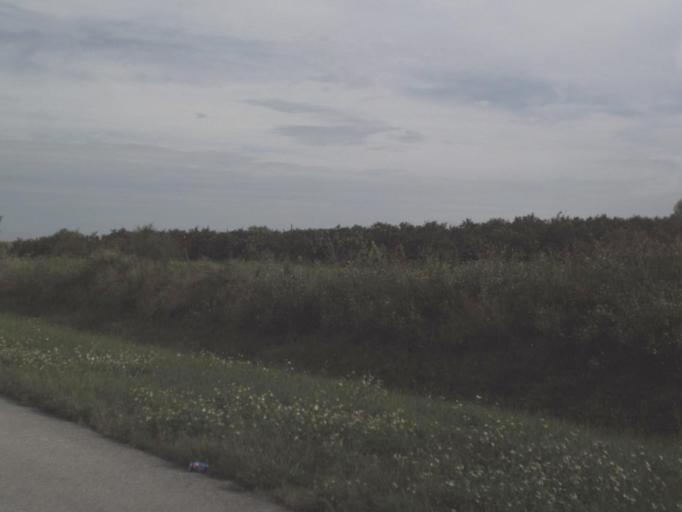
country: US
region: Florida
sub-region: DeSoto County
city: Nocatee
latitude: 27.0765
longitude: -81.7952
